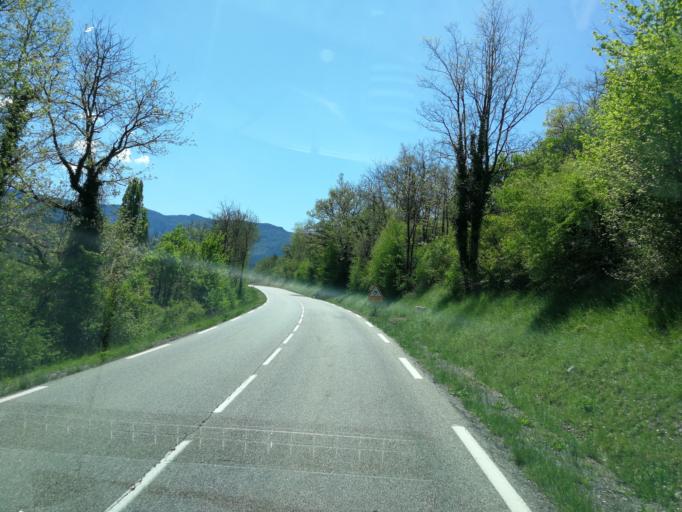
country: FR
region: Rhone-Alpes
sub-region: Departement de la Drome
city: Die
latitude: 44.7273
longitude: 5.2659
